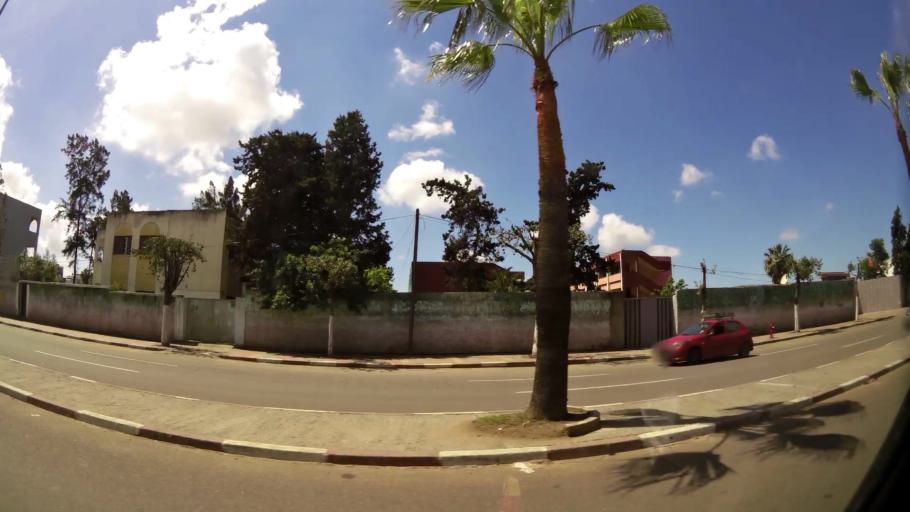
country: MA
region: Grand Casablanca
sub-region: Casablanca
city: Casablanca
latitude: 33.5581
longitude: -7.5876
